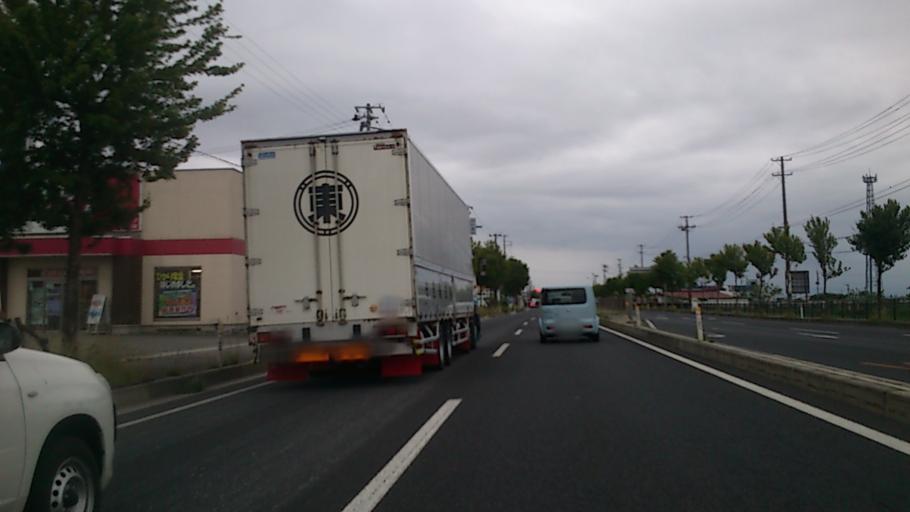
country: JP
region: Yamagata
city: Higashine
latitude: 38.4772
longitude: 140.3829
